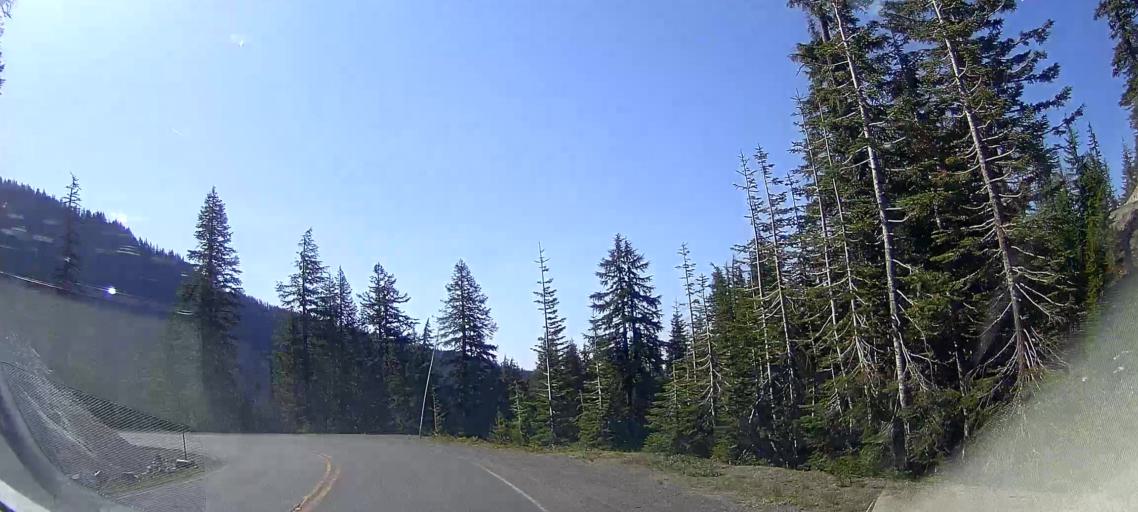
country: US
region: Oregon
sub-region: Jackson County
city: Shady Cove
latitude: 42.9031
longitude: -122.1375
